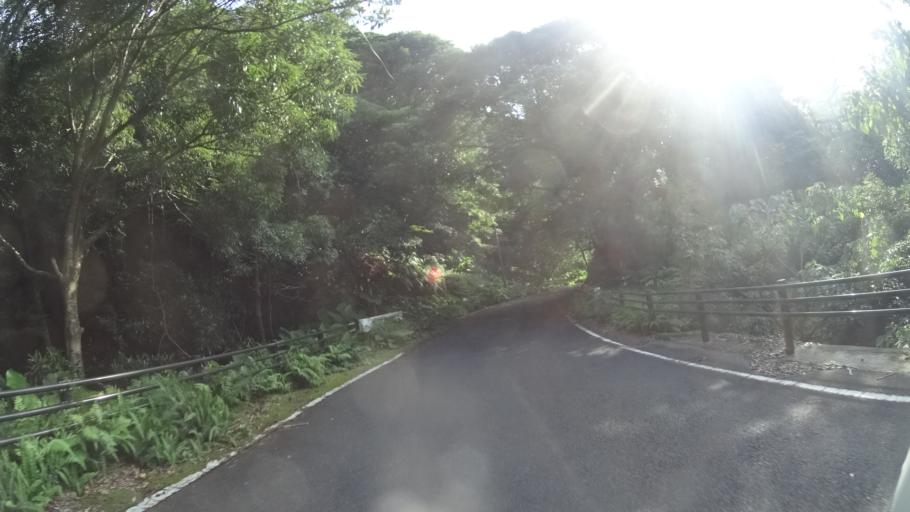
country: JP
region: Kagoshima
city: Nishinoomote
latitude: 30.3878
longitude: 130.3865
